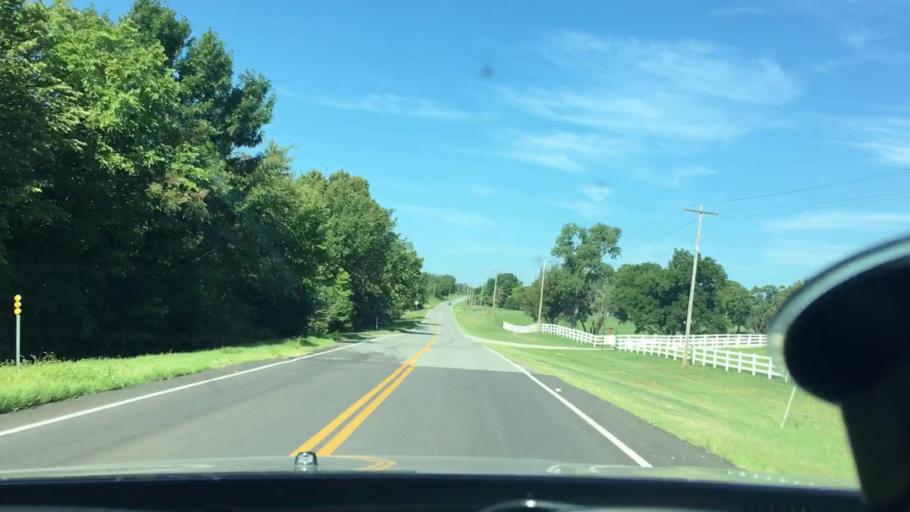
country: US
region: Oklahoma
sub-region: Johnston County
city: Tishomingo
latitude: 34.2744
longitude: -96.4832
